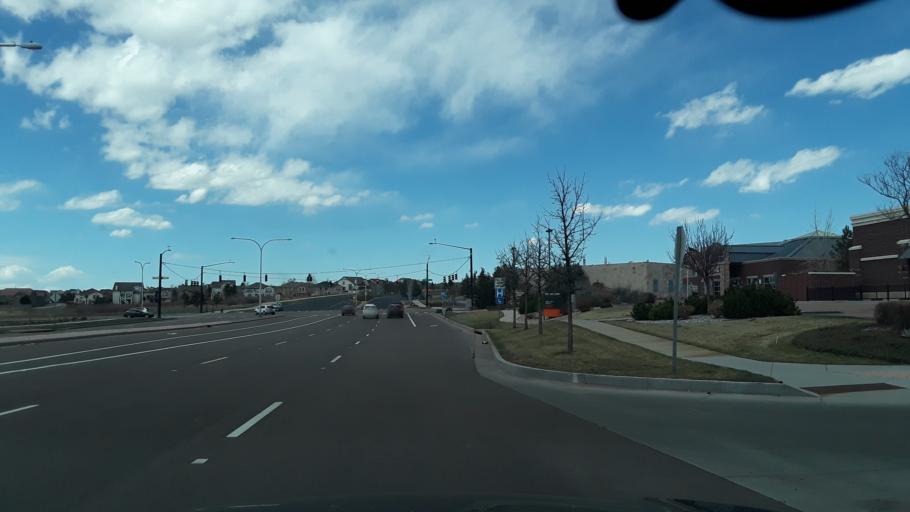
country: US
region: Colorado
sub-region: El Paso County
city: Black Forest
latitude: 38.9646
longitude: -104.7574
